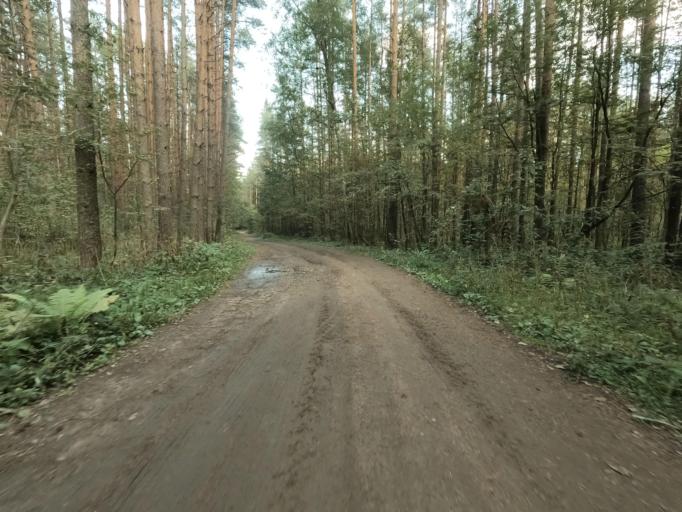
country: RU
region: Leningrad
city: Imeni Sverdlova
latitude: 59.8384
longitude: 30.7161
